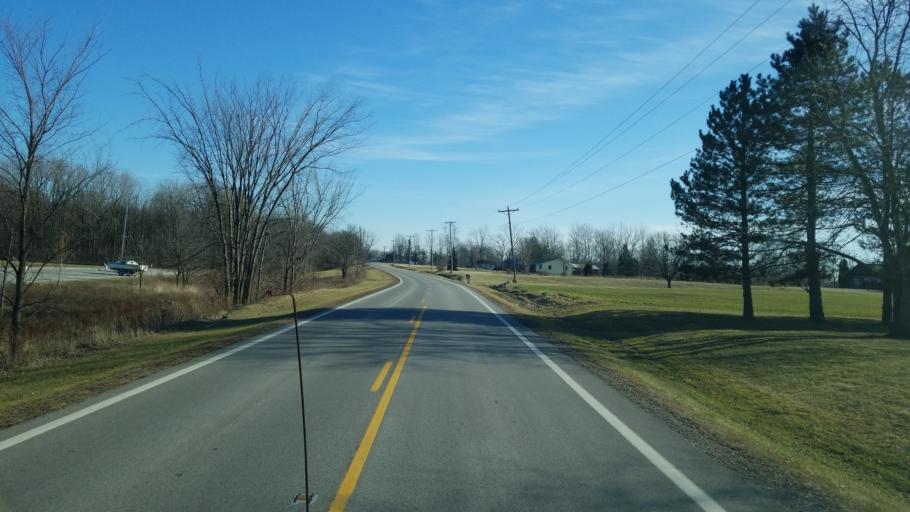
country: US
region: Ohio
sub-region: Wood County
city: Weston
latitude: 41.4110
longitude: -83.8890
